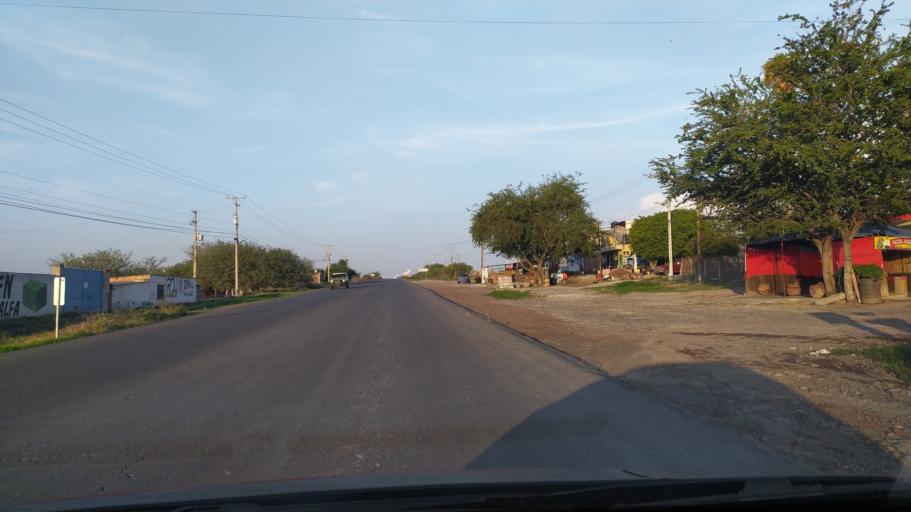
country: MX
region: Michoacan
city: Vistahermosa de Negrete
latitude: 20.2662
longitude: -102.4679
